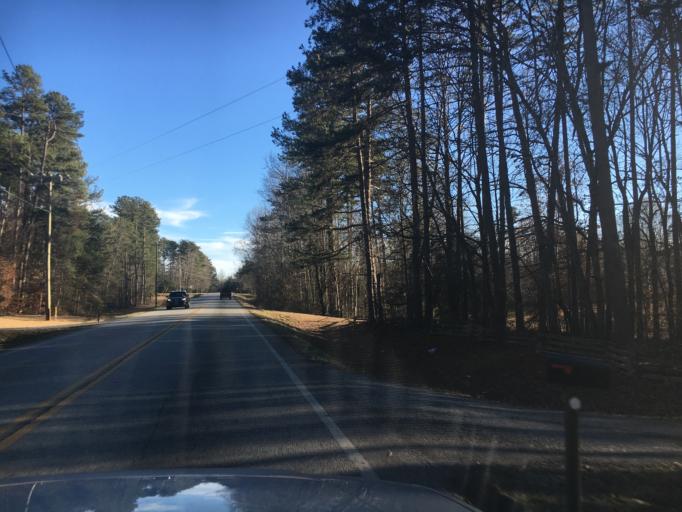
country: US
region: Georgia
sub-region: Habersham County
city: Demorest
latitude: 34.5568
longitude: -83.5743
